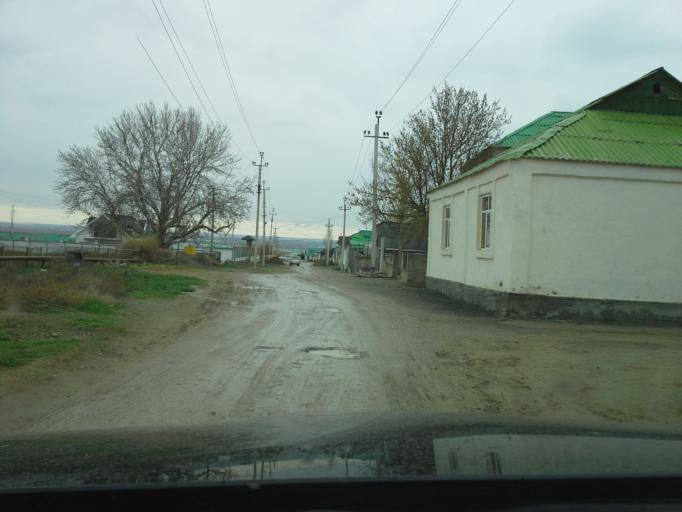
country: TM
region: Ahal
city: Abadan
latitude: 37.9565
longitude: 58.1999
